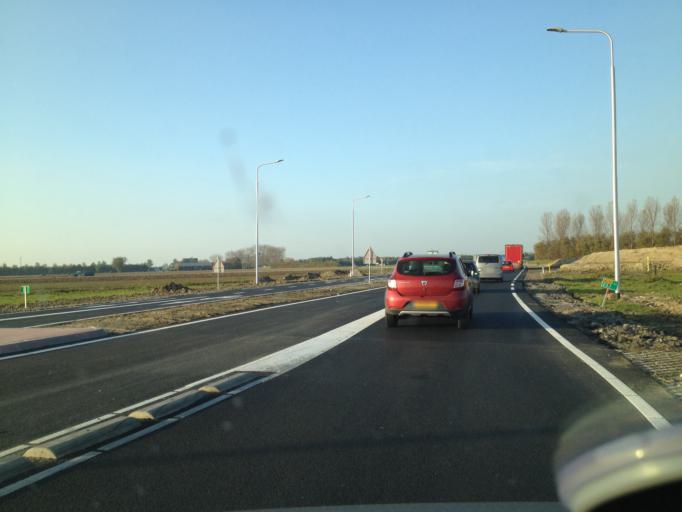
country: NL
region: Zeeland
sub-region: Gemeente Terneuzen
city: Sluiskil
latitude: 51.2961
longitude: 3.8634
